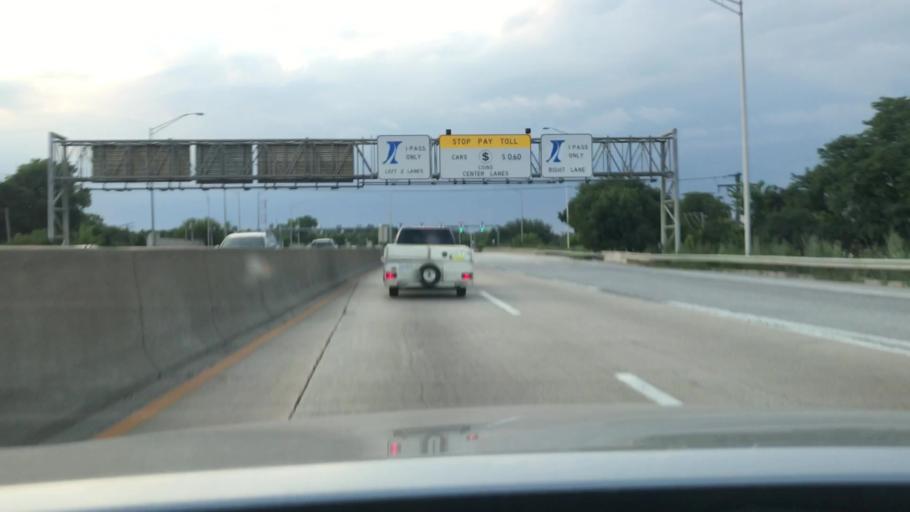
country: US
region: Illinois
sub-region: Cook County
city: Indian Head Park
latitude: 41.7636
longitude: -87.9054
